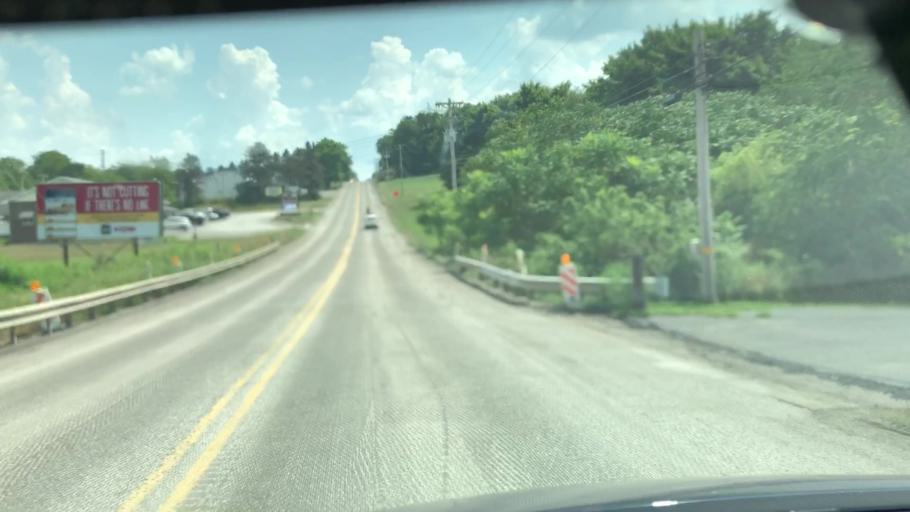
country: US
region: Pennsylvania
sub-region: Butler County
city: Saxonburg
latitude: 40.7938
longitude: -79.8142
